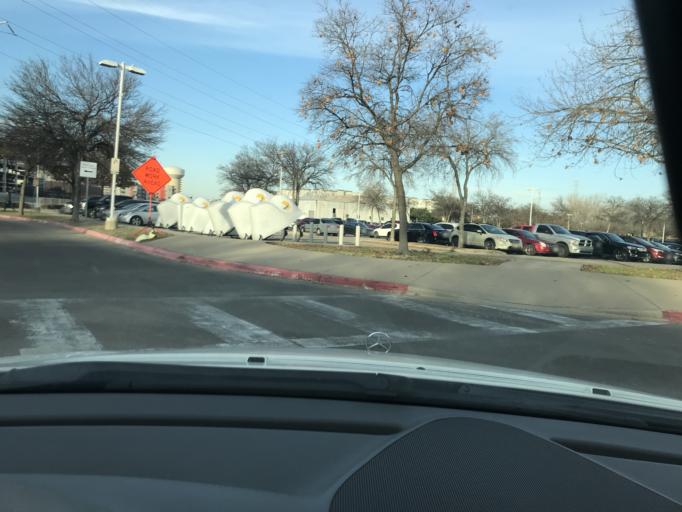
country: US
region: Texas
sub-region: Dallas County
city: Highland Park
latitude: 32.8379
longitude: -96.7736
